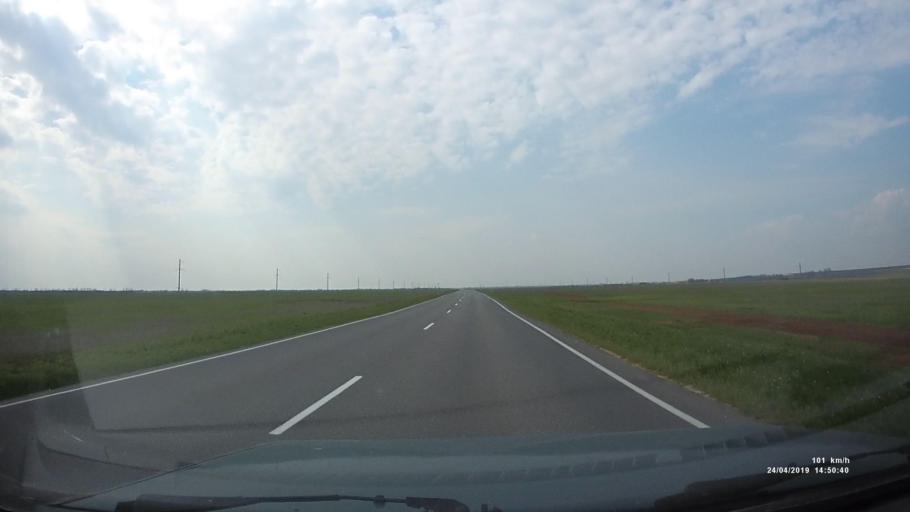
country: RU
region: Rostov
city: Remontnoye
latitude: 46.5191
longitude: 43.7151
